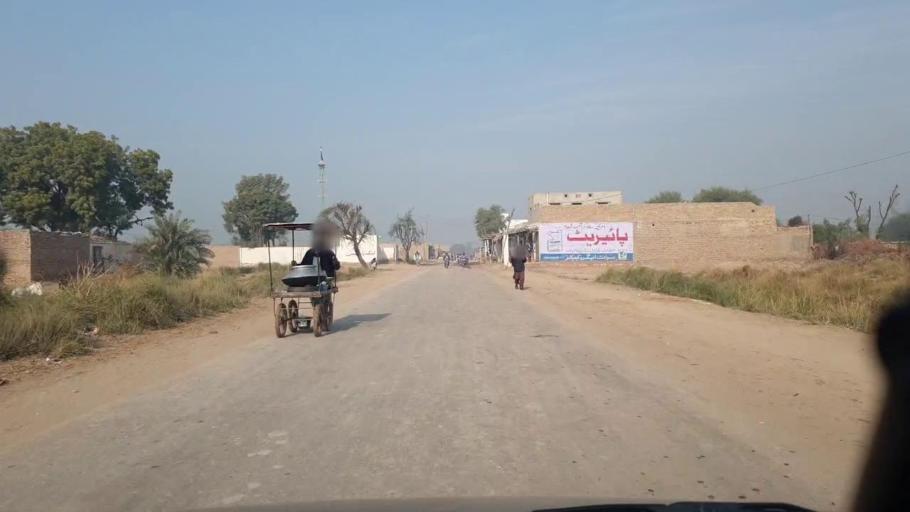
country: PK
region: Sindh
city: Shahdadpur
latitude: 25.9326
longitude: 68.6113
